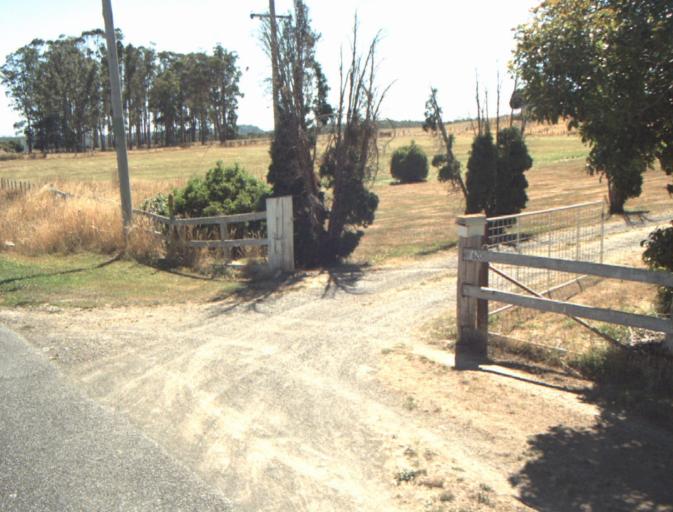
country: AU
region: Tasmania
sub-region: Launceston
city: Newstead
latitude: -41.3396
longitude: 147.3031
